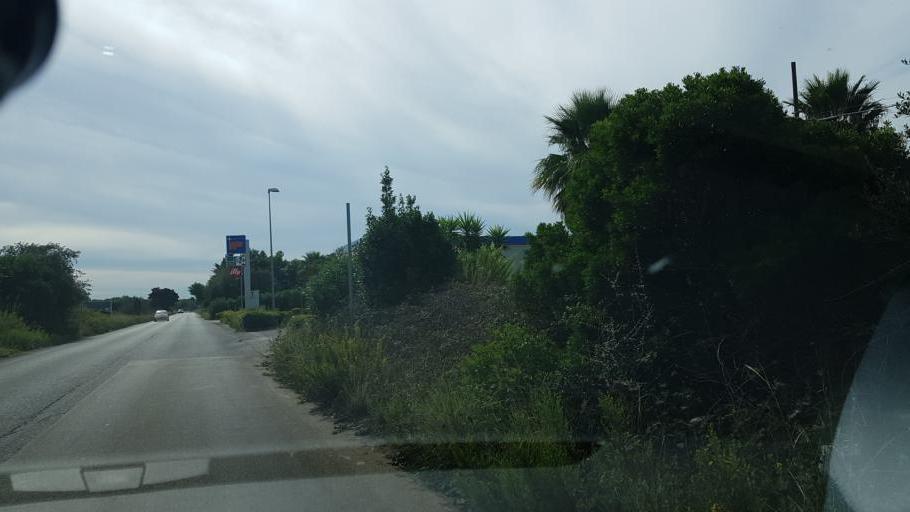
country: IT
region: Apulia
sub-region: Provincia di Lecce
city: Borgagne
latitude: 40.2579
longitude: 18.4363
